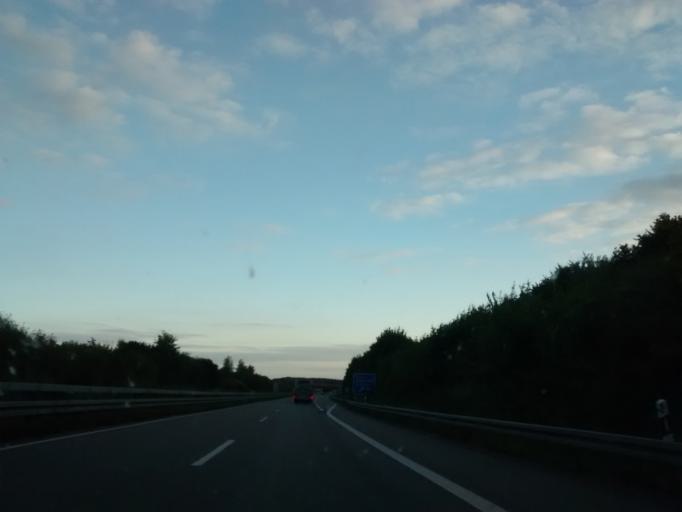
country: DE
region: Lower Saxony
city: Bad Rothenfelde
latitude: 52.1227
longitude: 8.1781
